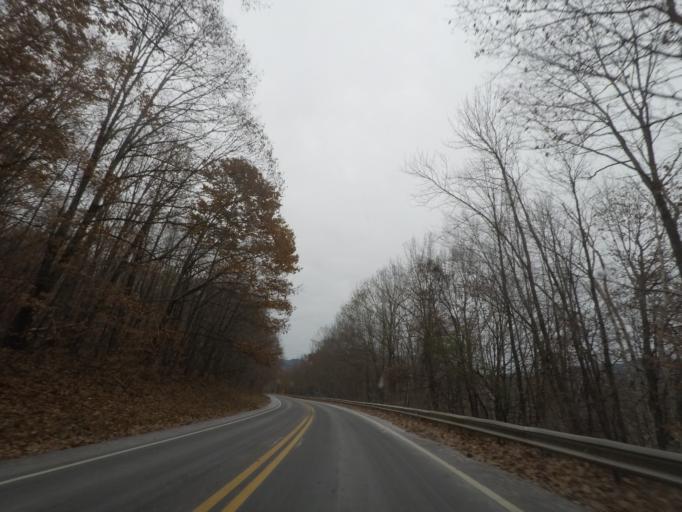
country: US
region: Massachusetts
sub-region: Berkshire County
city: Williamstown
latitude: 42.6928
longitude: -73.2393
